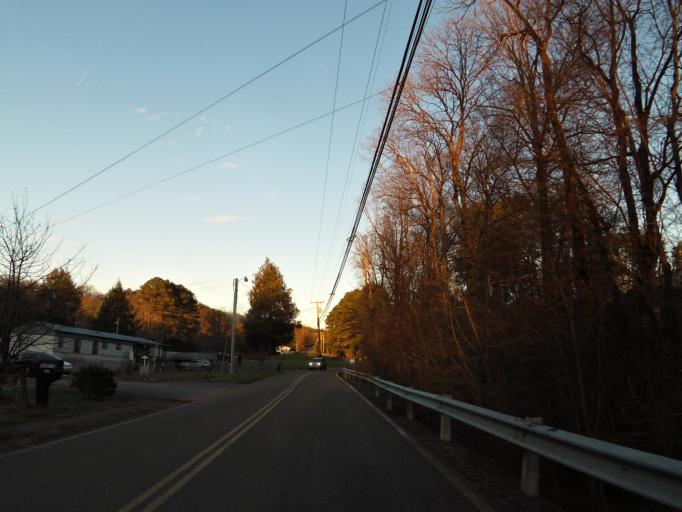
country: US
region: Tennessee
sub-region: Blount County
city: Eagleton Village
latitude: 35.8319
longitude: -83.9342
